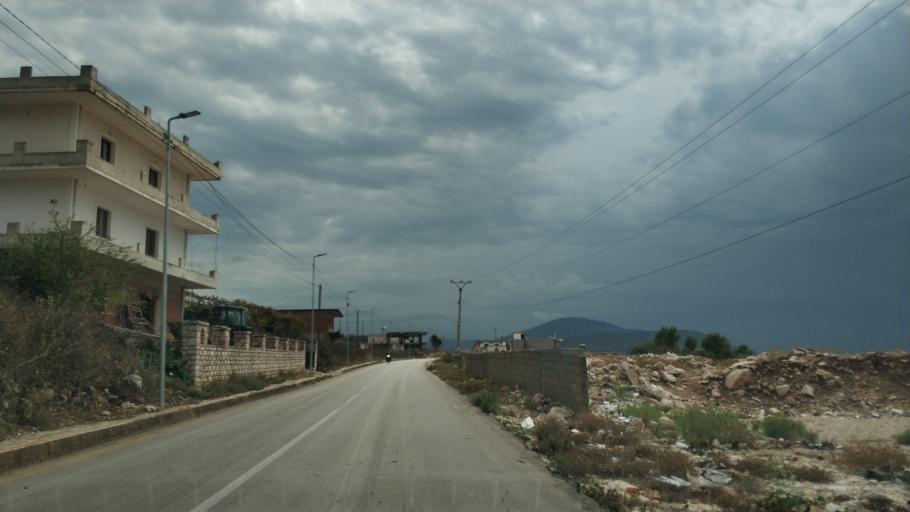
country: AL
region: Vlore
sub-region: Rrethi i Sarandes
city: Sarande
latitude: 39.8485
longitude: 20.0297
